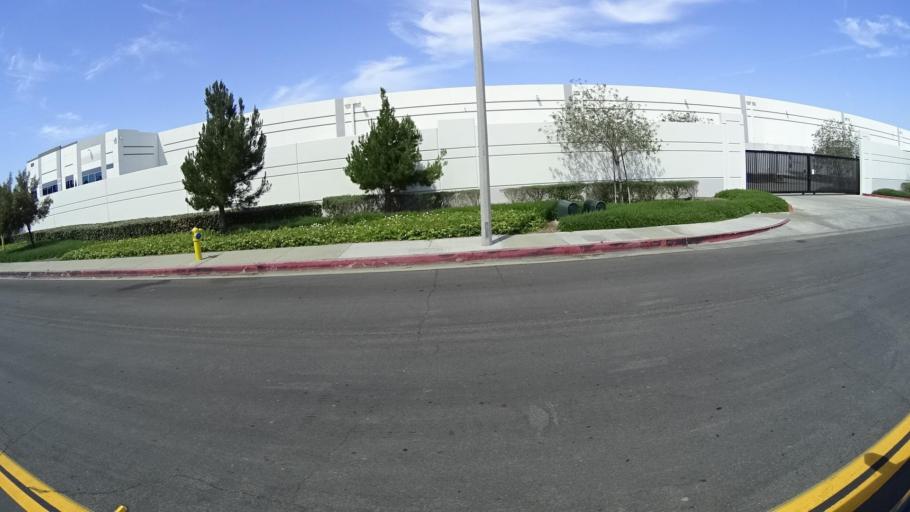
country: US
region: California
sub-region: Los Angeles County
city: South San Jose Hills
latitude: 34.0029
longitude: -117.9136
